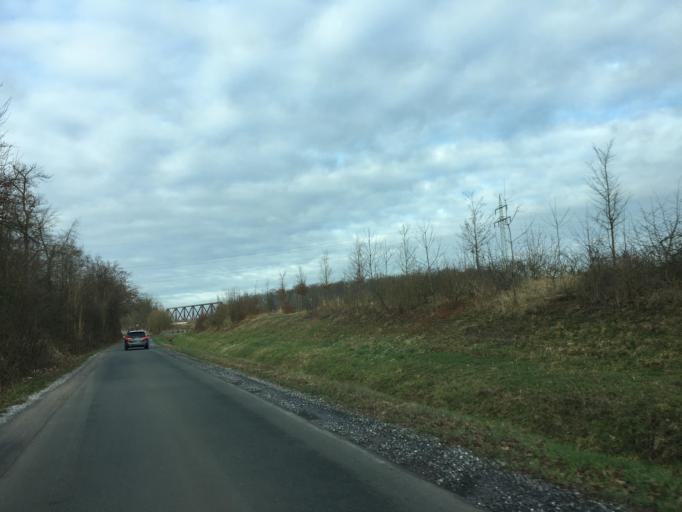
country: DE
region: North Rhine-Westphalia
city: Ludinghausen
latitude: 51.7734
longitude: 7.4144
